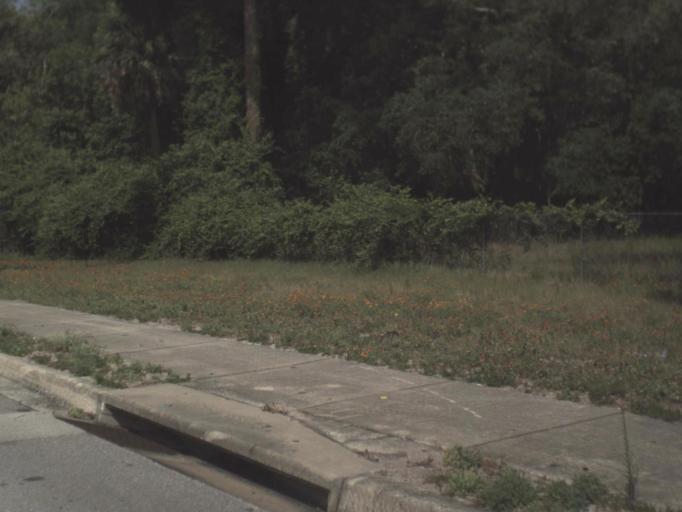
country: US
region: Florida
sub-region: Saint Johns County
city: Saint Augustine South
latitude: 29.8493
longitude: -81.3595
